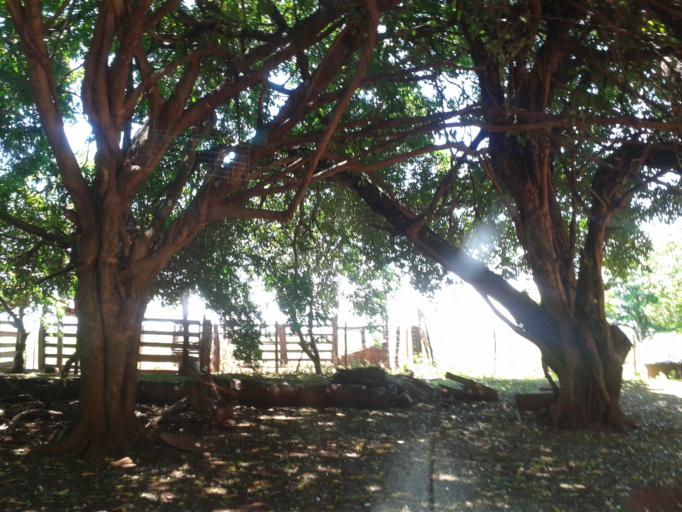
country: BR
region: Minas Gerais
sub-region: Centralina
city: Centralina
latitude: -18.6238
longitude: -49.2770
